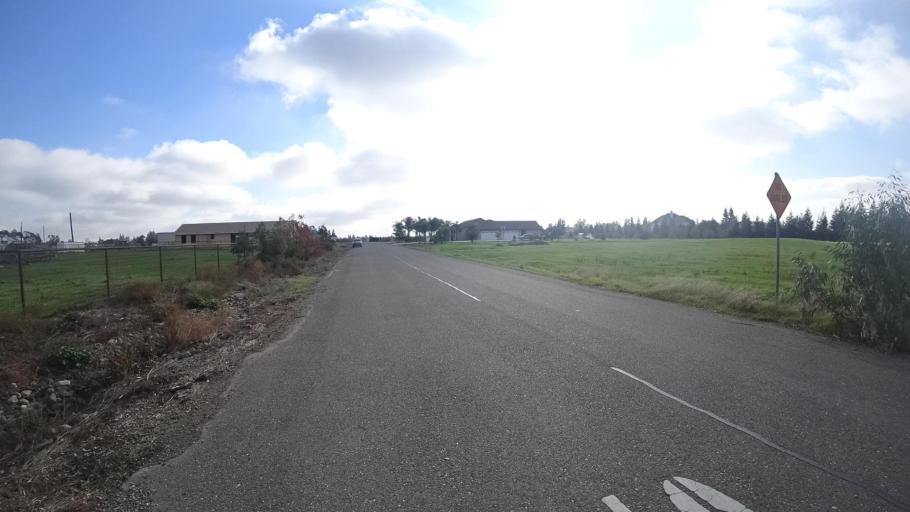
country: US
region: California
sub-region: Sacramento County
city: Vineyard
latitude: 38.4343
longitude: -121.3405
